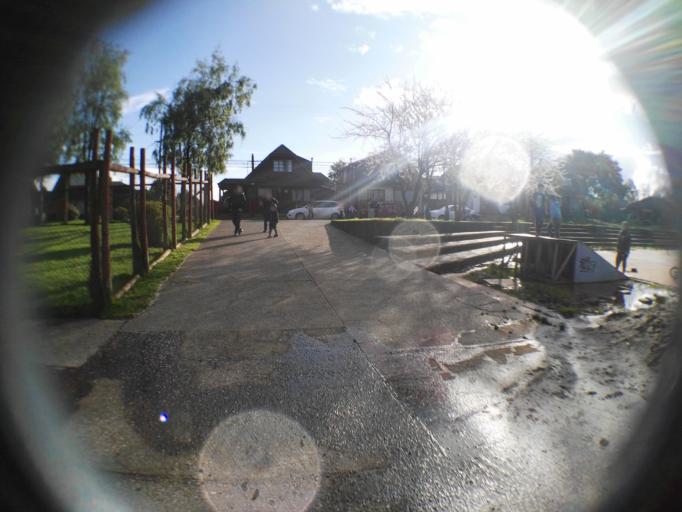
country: CL
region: Los Rios
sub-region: Provincia de Valdivia
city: Valdivia
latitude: -39.8330
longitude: -73.2285
